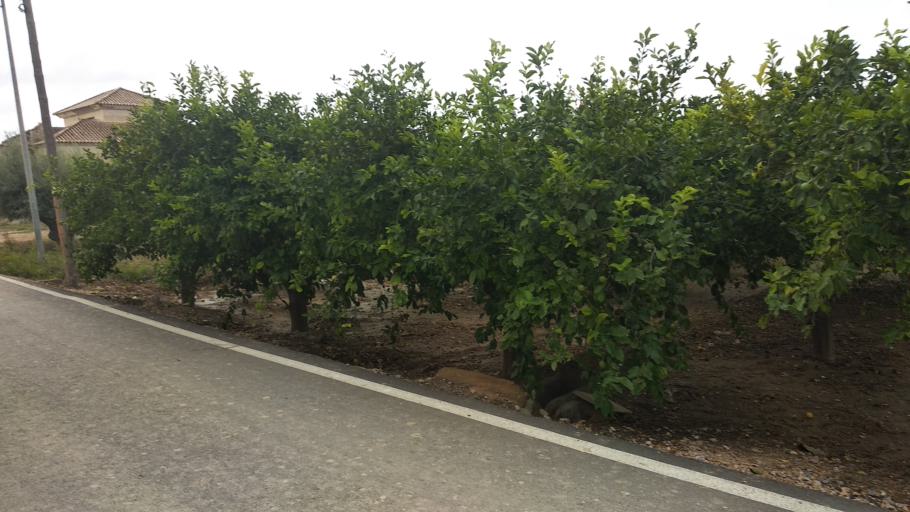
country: ES
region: Murcia
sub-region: Murcia
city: Santomera
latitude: 38.0402
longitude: -1.0336
